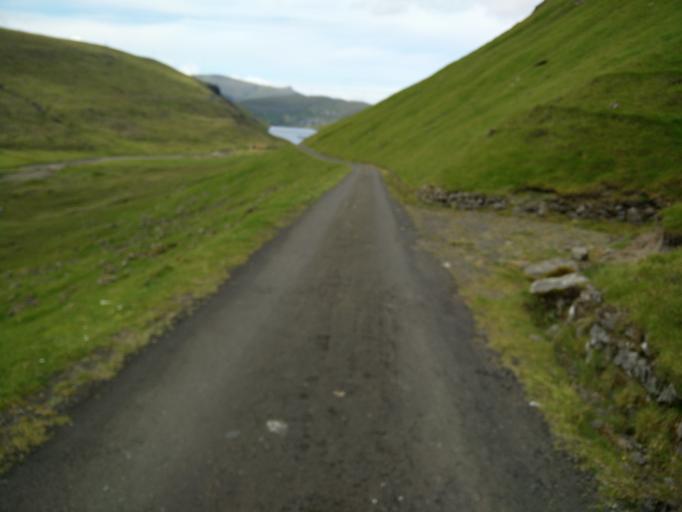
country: FO
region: Streymoy
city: Vestmanna
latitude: 62.1545
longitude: -7.0865
